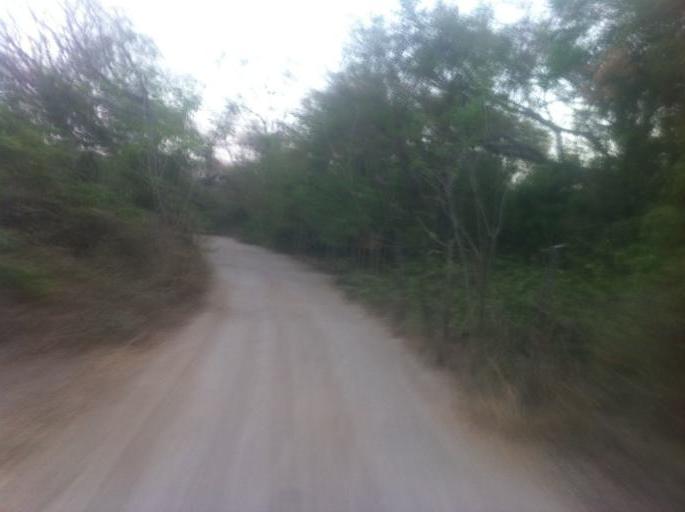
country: CR
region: Guanacaste
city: Samara
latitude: 9.9426
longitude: -85.6676
